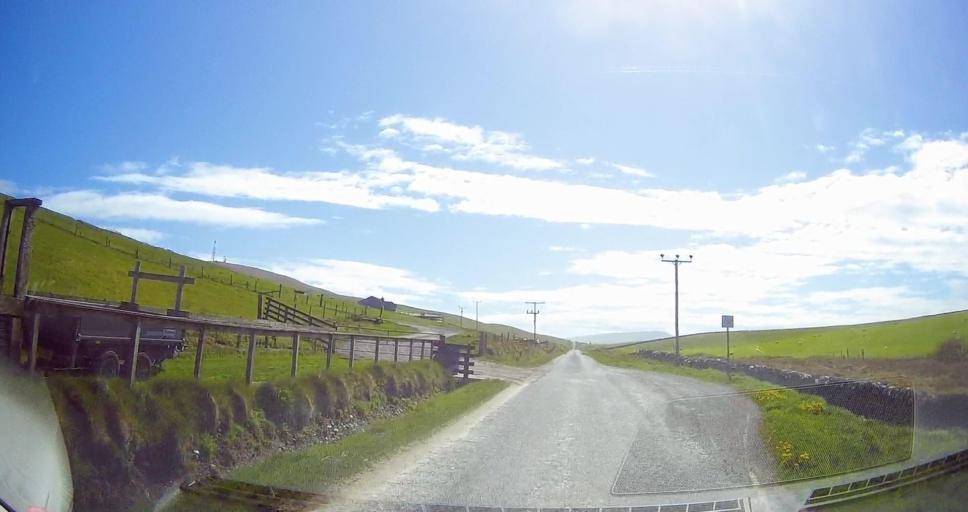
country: GB
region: Scotland
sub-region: Shetland Islands
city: Sandwick
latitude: 59.9710
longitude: -1.3168
